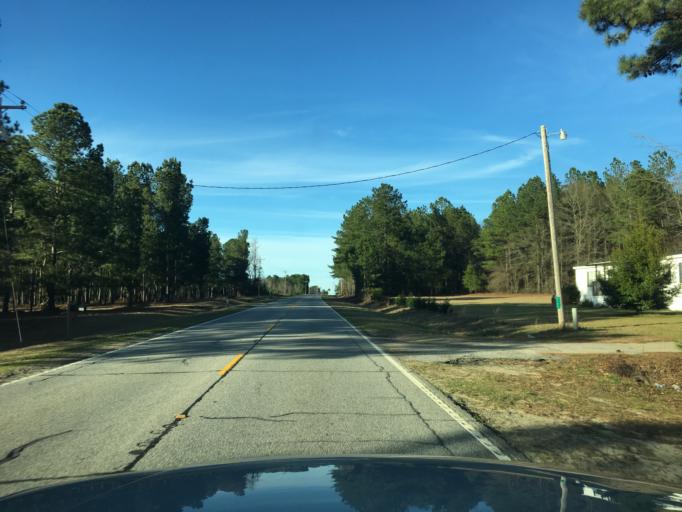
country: US
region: South Carolina
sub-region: Edgefield County
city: Johnston
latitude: 33.7575
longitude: -81.6428
